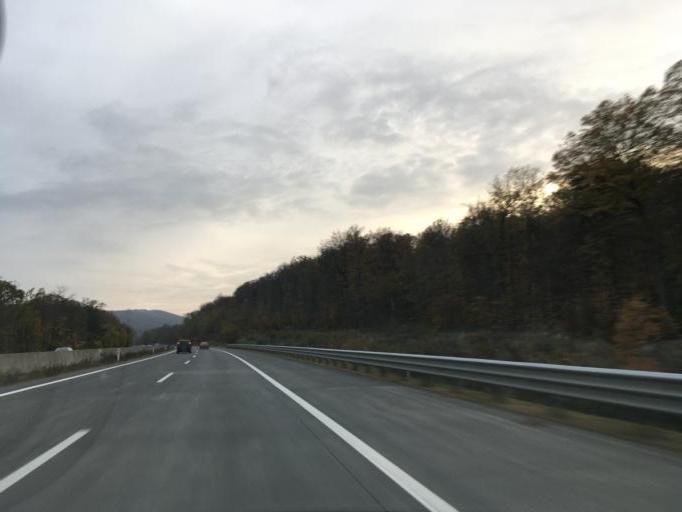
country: AT
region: Lower Austria
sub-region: Politischer Bezirk Wien-Umgebung
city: Purkersdorf
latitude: 48.1904
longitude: 16.1957
